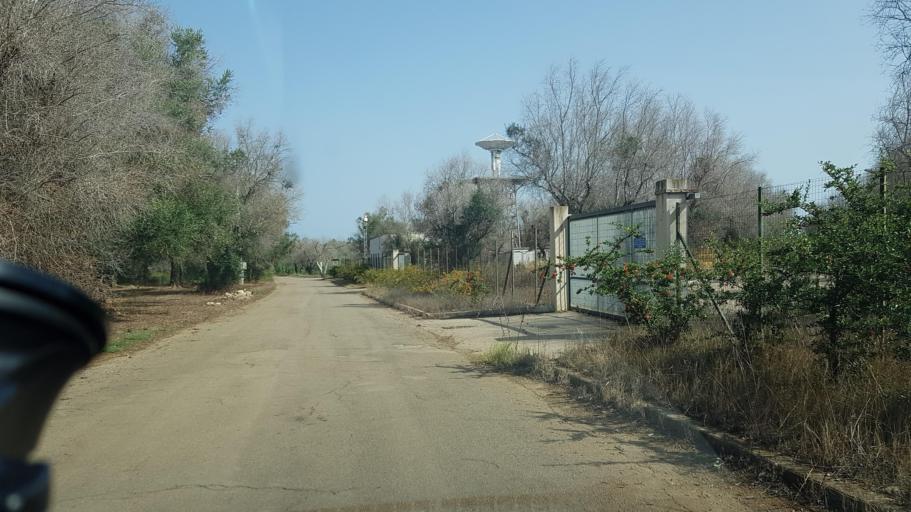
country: IT
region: Apulia
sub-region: Provincia di Brindisi
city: Torchiarolo
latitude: 40.5058
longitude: 18.0593
